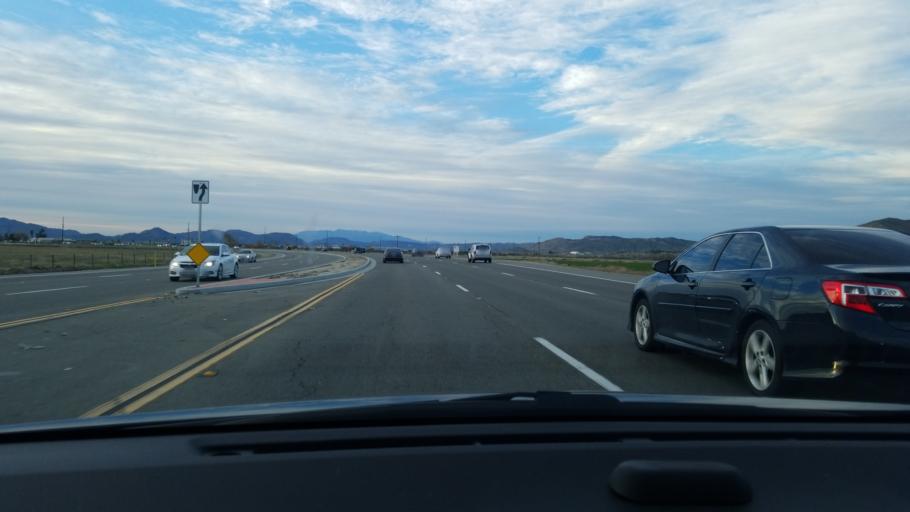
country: US
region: California
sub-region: Riverside County
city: San Jacinto
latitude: 33.8210
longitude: -116.9975
